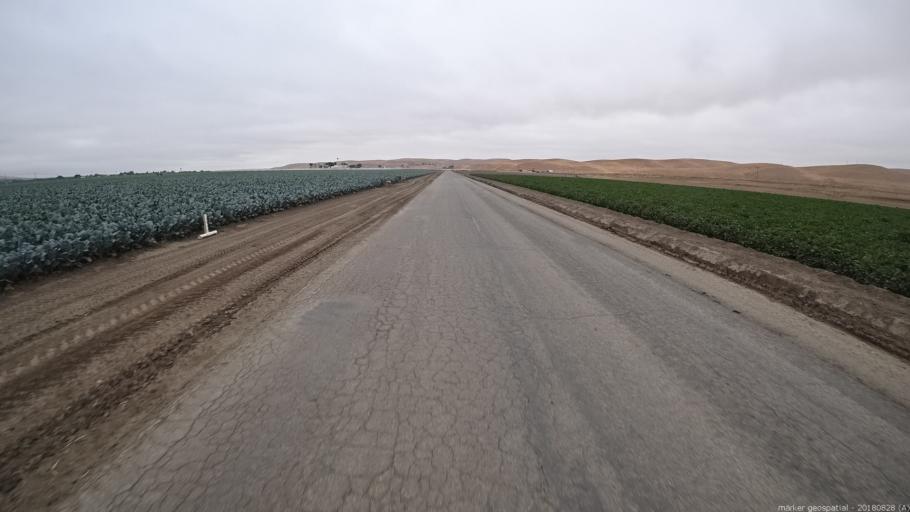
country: US
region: California
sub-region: San Luis Obispo County
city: Lake Nacimiento
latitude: 36.0025
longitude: -120.8862
